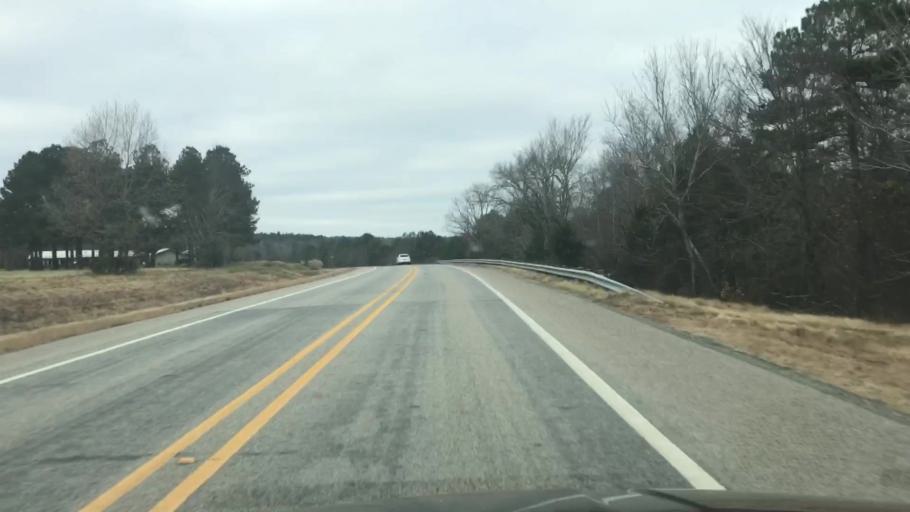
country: US
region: Arkansas
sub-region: Scott County
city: Waldron
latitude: 34.7028
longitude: -93.9203
